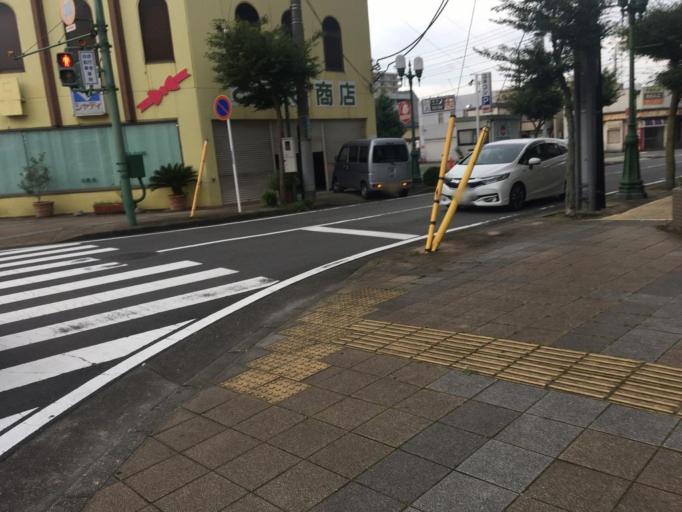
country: JP
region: Gunma
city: Isesaki
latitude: 36.3204
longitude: 139.1948
